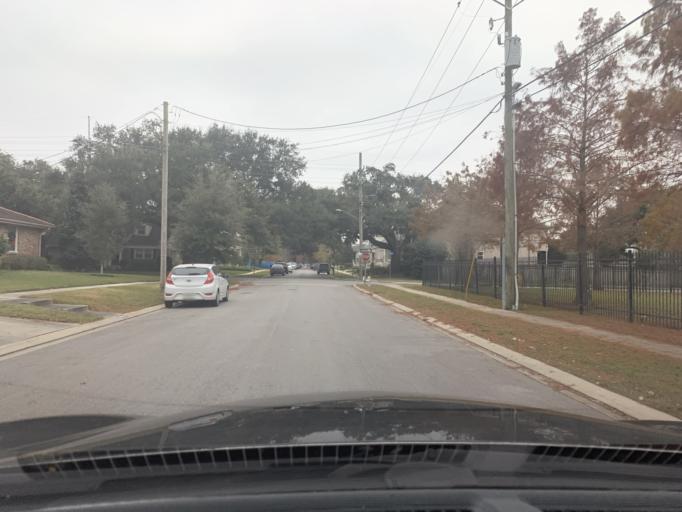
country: US
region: Louisiana
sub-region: Jefferson Parish
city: Metairie
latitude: 30.0183
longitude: -90.1088
